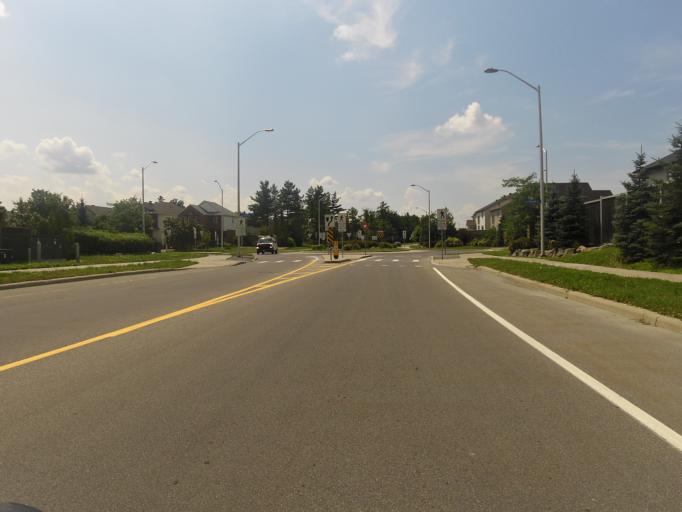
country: CA
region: Ontario
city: Bells Corners
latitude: 45.3207
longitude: -75.9271
